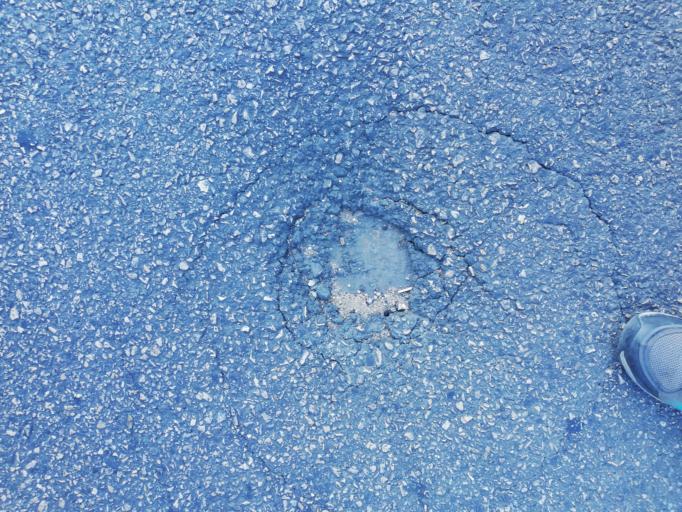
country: LB
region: Mont-Liban
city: Jdaidet el Matn
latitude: 33.8988
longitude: 35.5919
